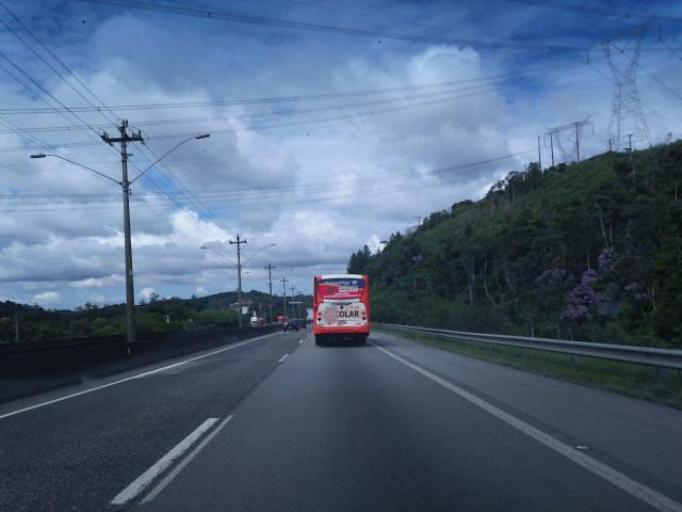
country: BR
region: Sao Paulo
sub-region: Sao Lourenco Da Serra
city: Sao Lourenco da Serra
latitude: -23.8880
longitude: -46.9792
